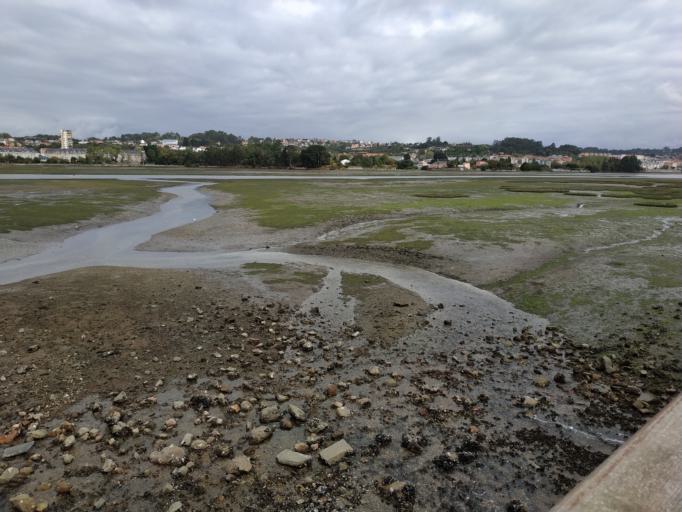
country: ES
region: Galicia
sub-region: Provincia da Coruna
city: Culleredo
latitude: 43.3238
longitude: -8.3772
